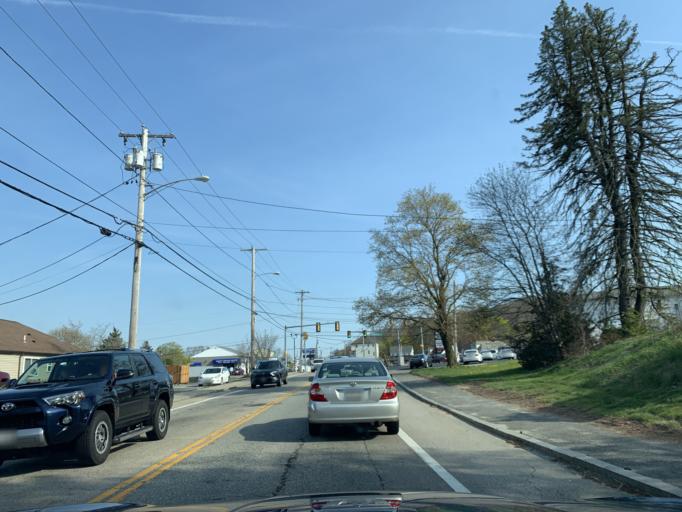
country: US
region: Rhode Island
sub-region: Providence County
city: Johnston
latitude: 41.8076
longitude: -71.4930
